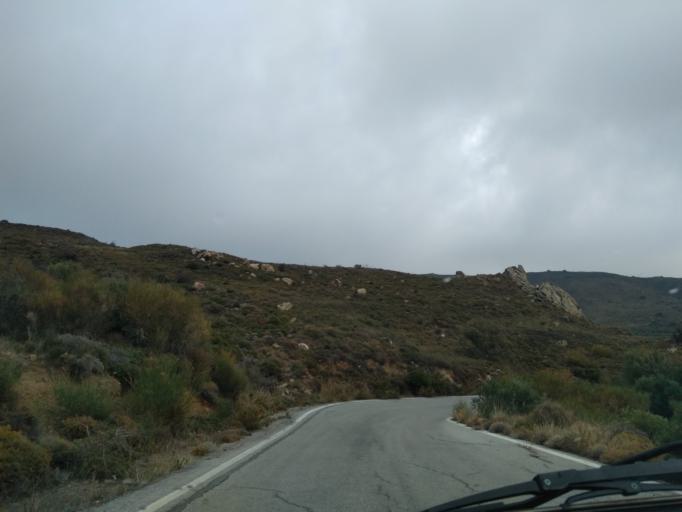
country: GR
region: Crete
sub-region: Nomos Lasithiou
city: Siteia
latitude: 35.1454
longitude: 26.0218
